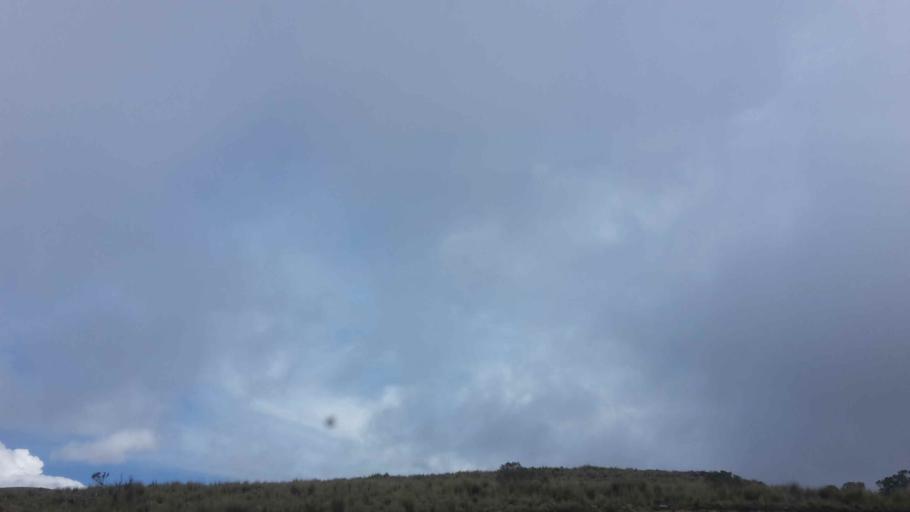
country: BO
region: Cochabamba
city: Cochabamba
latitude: -17.3290
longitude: -66.0801
